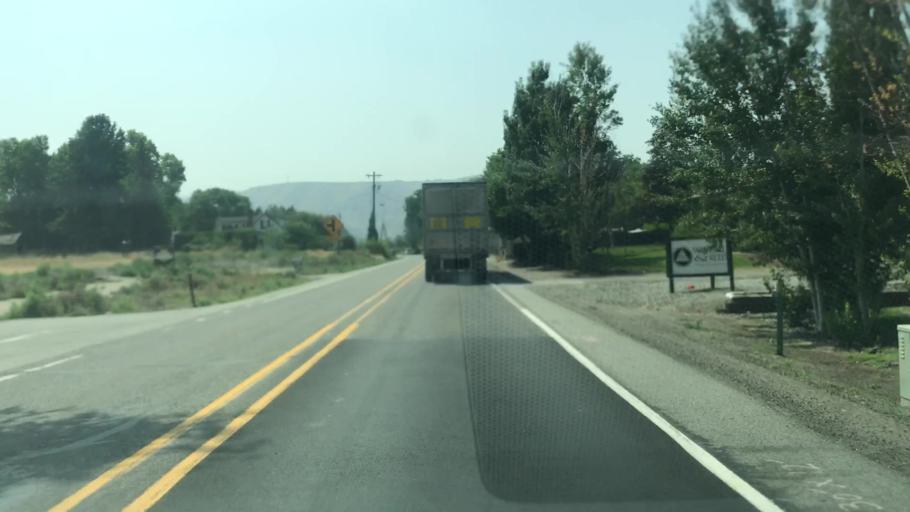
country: US
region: Washington
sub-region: Douglas County
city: East Wenatchee
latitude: 47.4262
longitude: -120.2978
